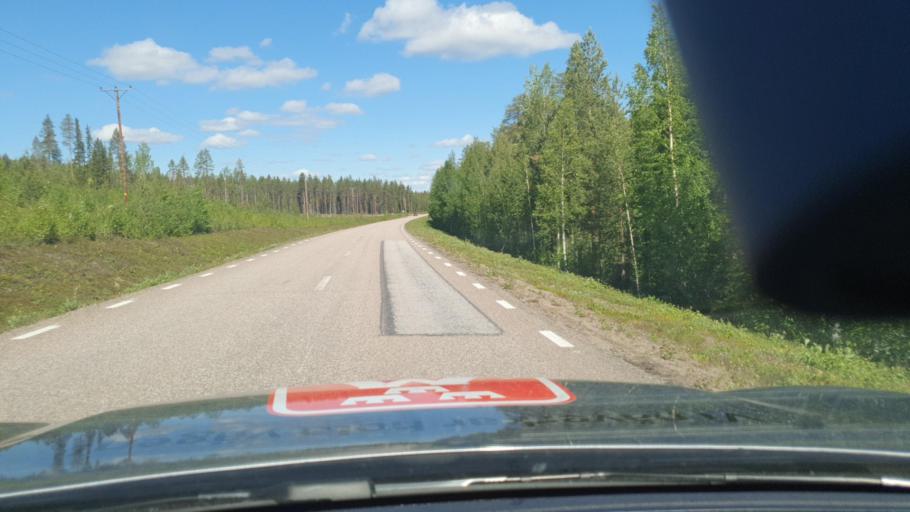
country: SE
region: Norrbotten
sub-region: Overkalix Kommun
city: OEverkalix
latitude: 67.0326
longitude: 22.5063
